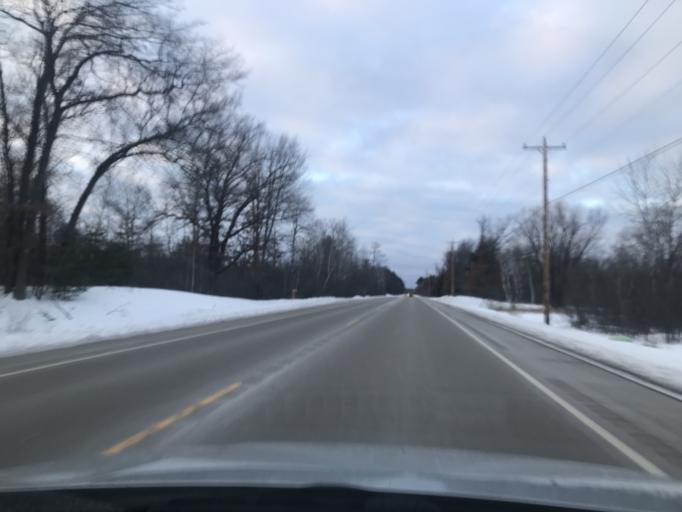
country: US
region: Wisconsin
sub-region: Marinette County
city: Marinette
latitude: 45.1242
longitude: -87.6842
